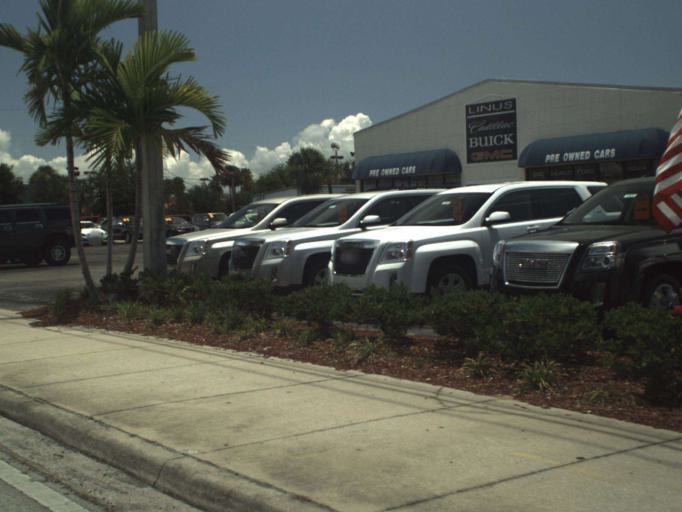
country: US
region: Florida
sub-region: Indian River County
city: Vero Beach
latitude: 27.6270
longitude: -80.3893
